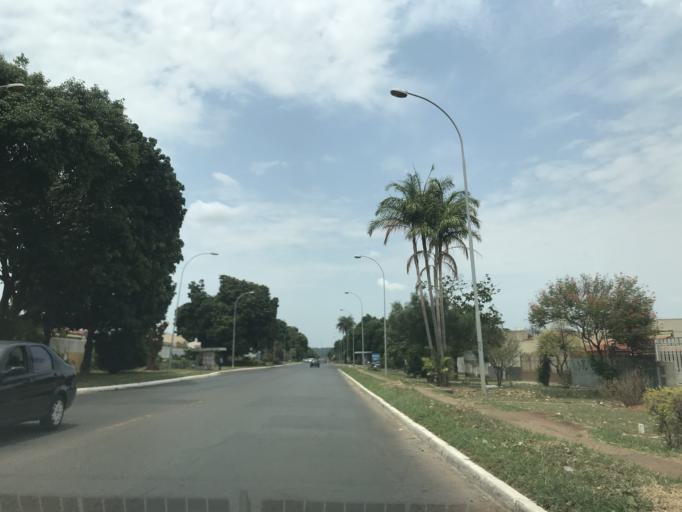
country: BR
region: Federal District
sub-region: Brasilia
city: Brasilia
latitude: -15.6526
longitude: -47.8043
